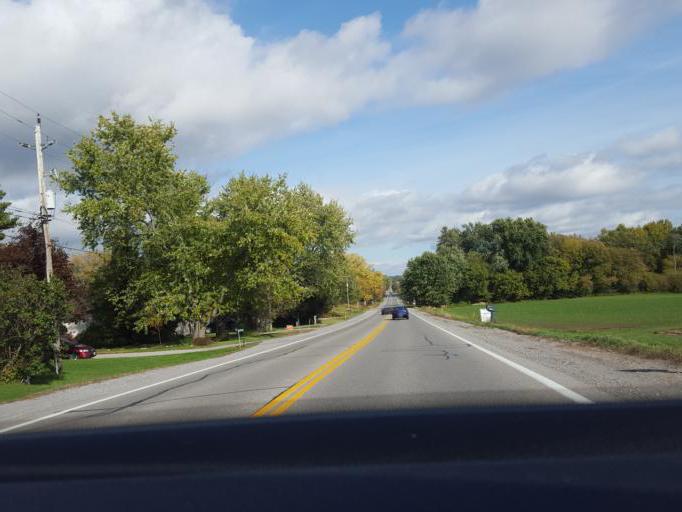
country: CA
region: Ontario
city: Oshawa
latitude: 43.9827
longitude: -78.6571
